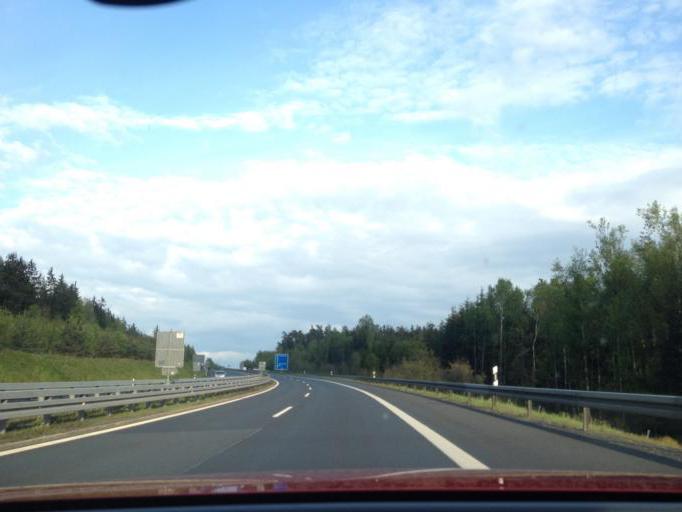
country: DE
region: Bavaria
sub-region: Upper Palatinate
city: Pechbrunn
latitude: 49.9537
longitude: 12.1963
